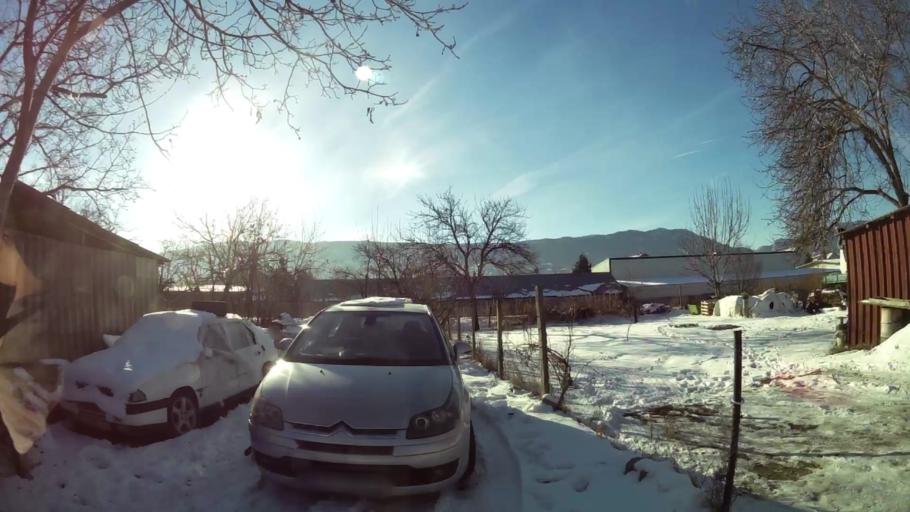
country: MK
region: Saraj
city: Saraj
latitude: 42.0114
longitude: 21.3437
